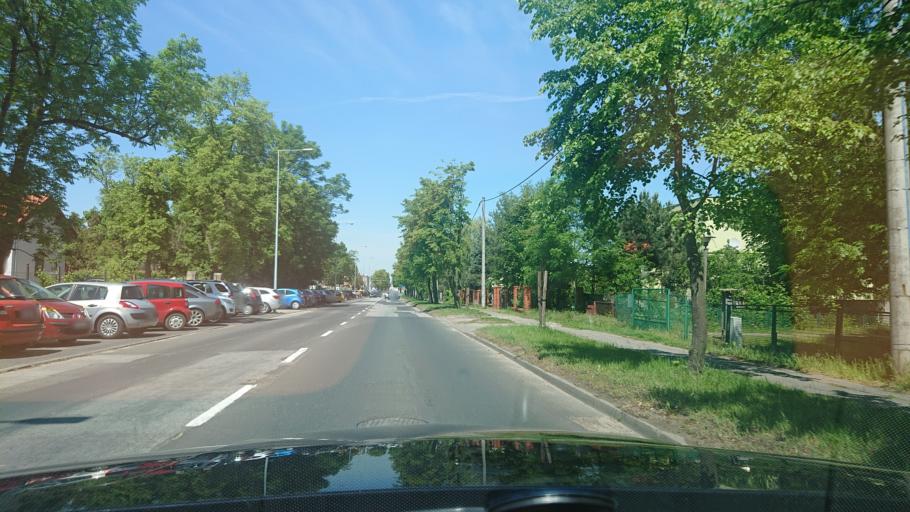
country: PL
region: Greater Poland Voivodeship
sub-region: Powiat gnieznienski
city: Gniezno
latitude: 52.5187
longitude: 17.6078
